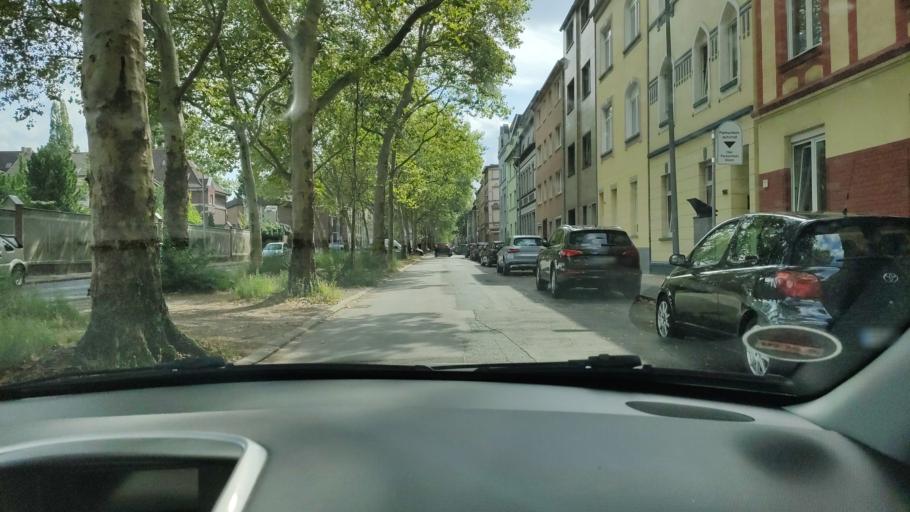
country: DE
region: North Rhine-Westphalia
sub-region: Regierungsbezirk Dusseldorf
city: Oberhausen
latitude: 51.4805
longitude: 6.8689
